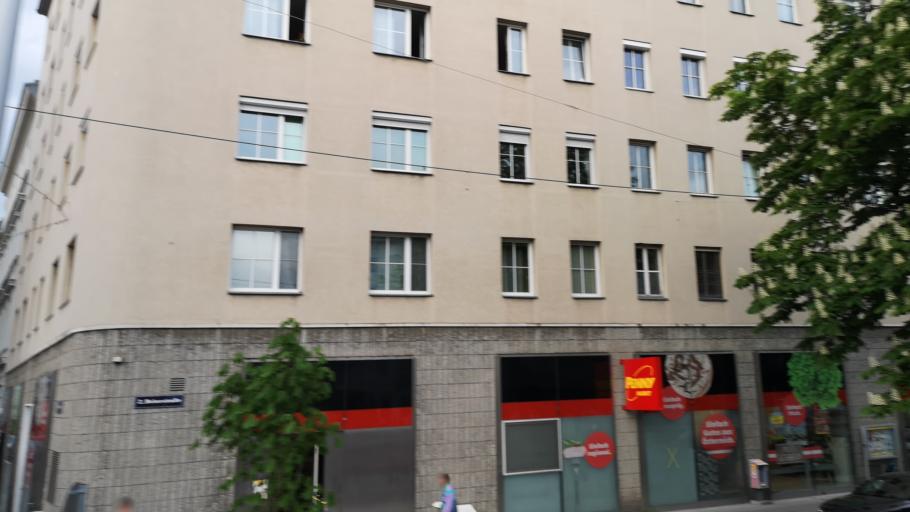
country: AT
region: Vienna
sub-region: Wien Stadt
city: Vienna
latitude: 48.2198
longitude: 16.3873
